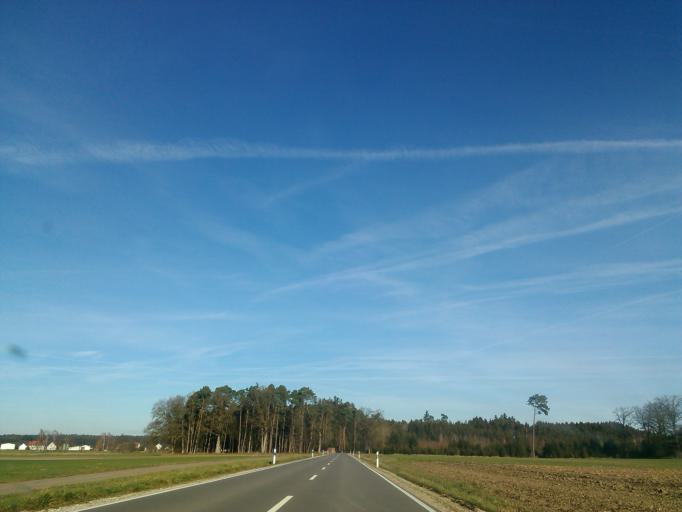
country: DE
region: Bavaria
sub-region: Swabia
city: Inchenhofen
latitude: 48.5252
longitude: 11.1050
